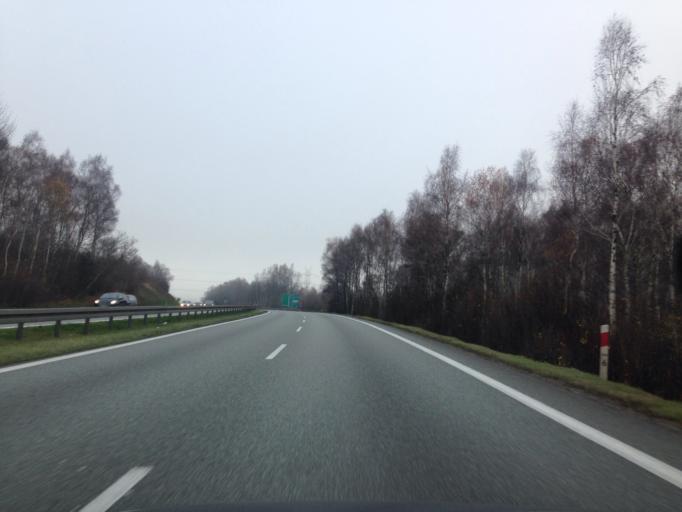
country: PL
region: Silesian Voivodeship
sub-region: Powiat bedzinski
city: Siewierz
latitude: 50.4370
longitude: 19.2155
